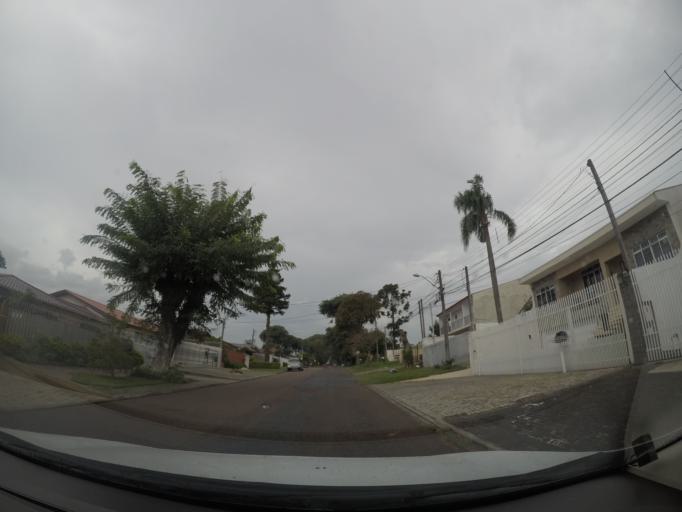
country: BR
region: Parana
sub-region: Sao Jose Dos Pinhais
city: Sao Jose dos Pinhais
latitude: -25.5123
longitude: -49.2473
